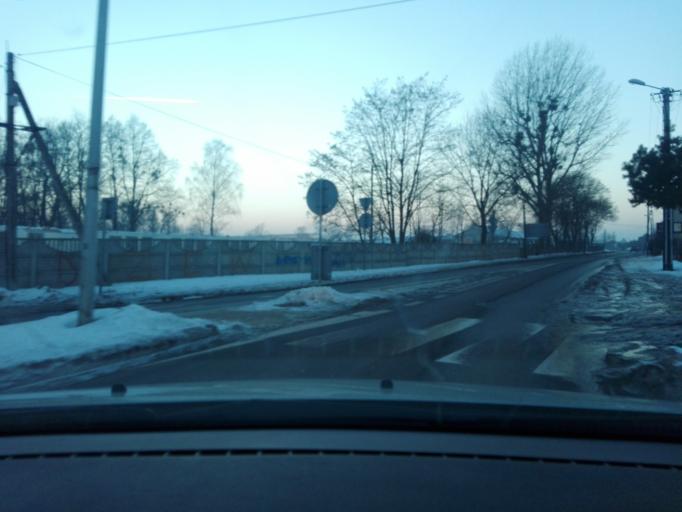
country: PL
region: Lodz Voivodeship
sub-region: Powiat zgierski
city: Zgierz
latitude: 51.8726
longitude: 19.4082
